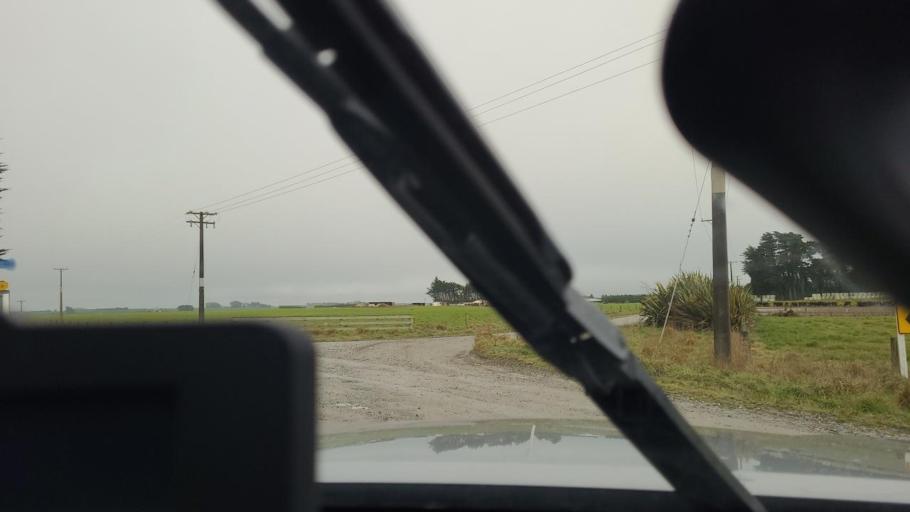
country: NZ
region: Southland
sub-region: Invercargill City
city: Invercargill
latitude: -46.4248
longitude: 168.6237
